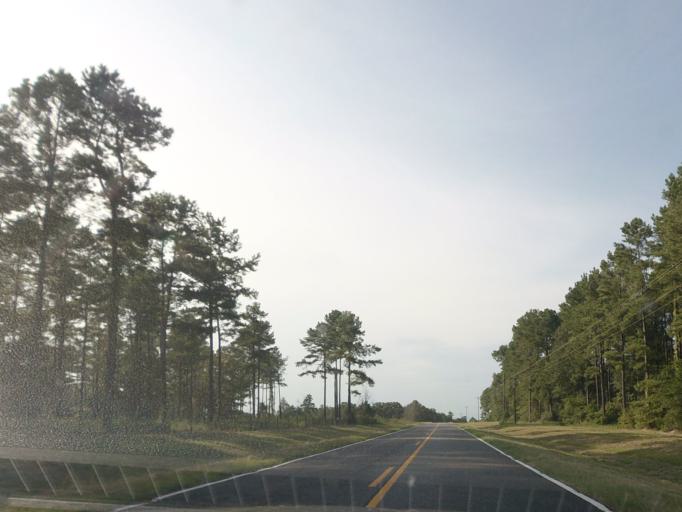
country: US
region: Georgia
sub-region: Bleckley County
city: Cochran
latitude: 32.4760
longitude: -83.3015
